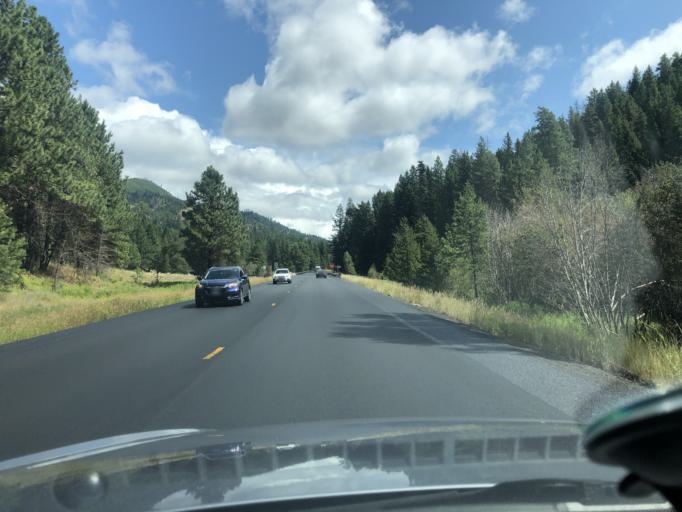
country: US
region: Washington
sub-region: Chelan County
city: Leavenworth
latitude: 47.3247
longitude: -120.6750
